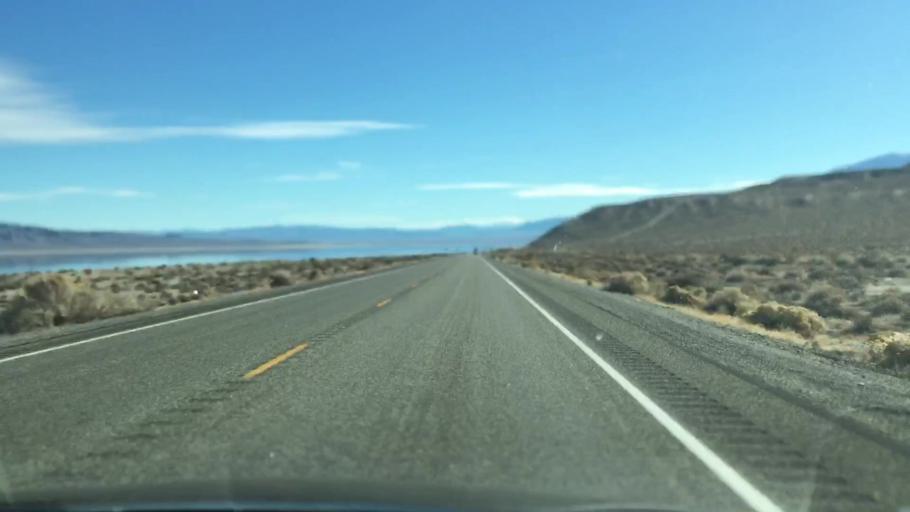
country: US
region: Nevada
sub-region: Mineral County
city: Hawthorne
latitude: 38.7891
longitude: -118.7545
